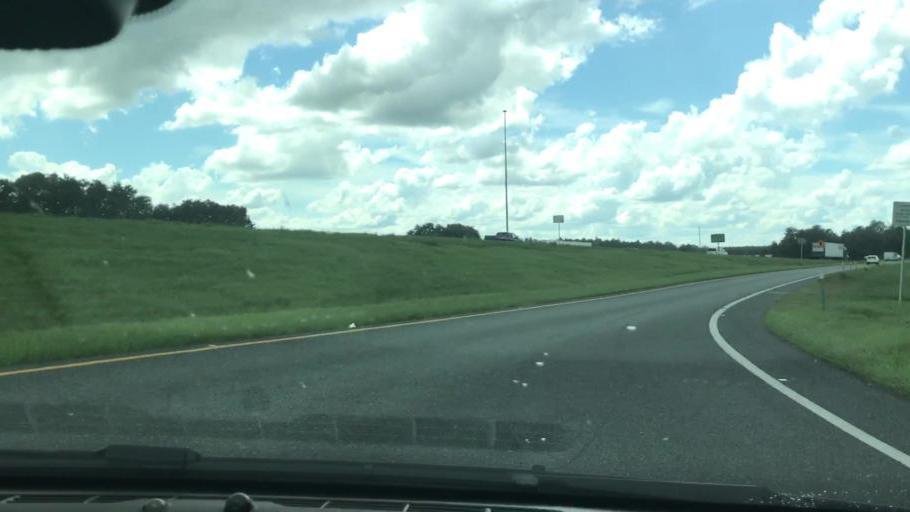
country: US
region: Florida
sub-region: Madison County
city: Madison
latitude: 30.3808
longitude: -83.2992
